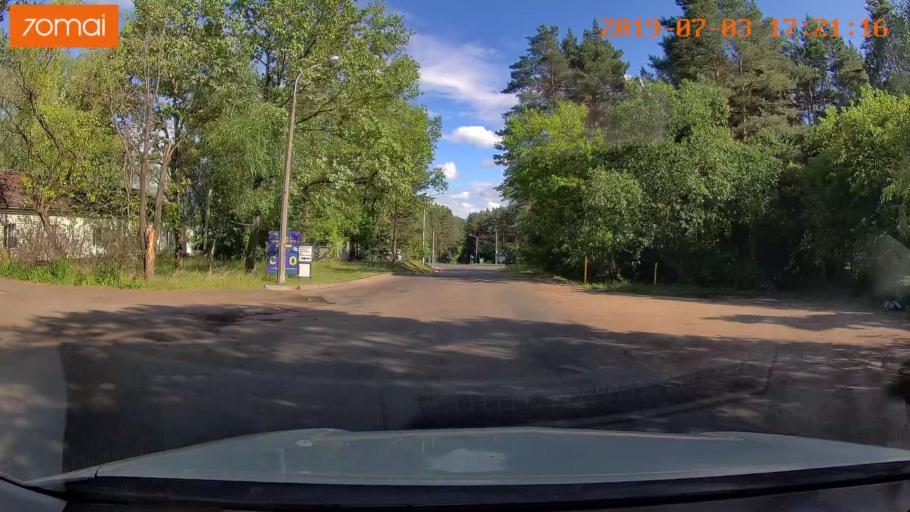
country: BY
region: Minsk
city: Vyaliki Trastsyanets
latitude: 53.9031
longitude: 27.6806
